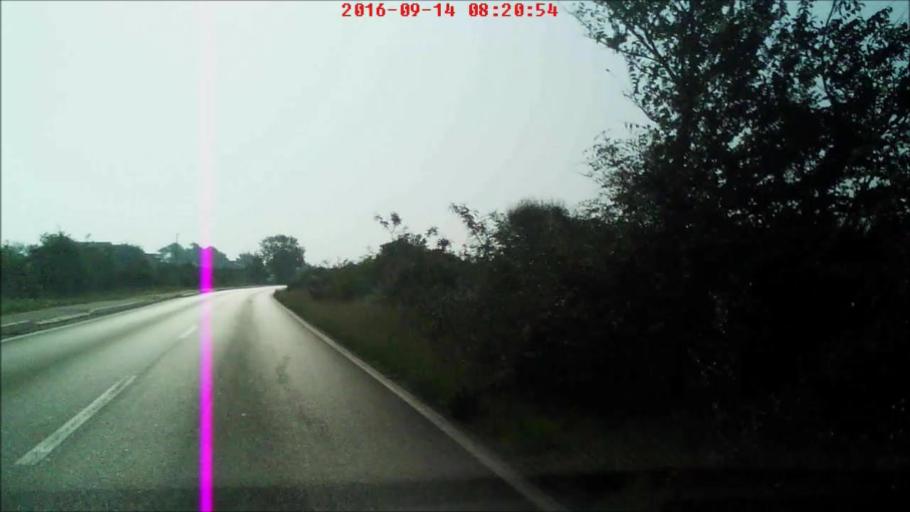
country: HR
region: Zadarska
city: Nin
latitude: 44.2247
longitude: 15.2055
